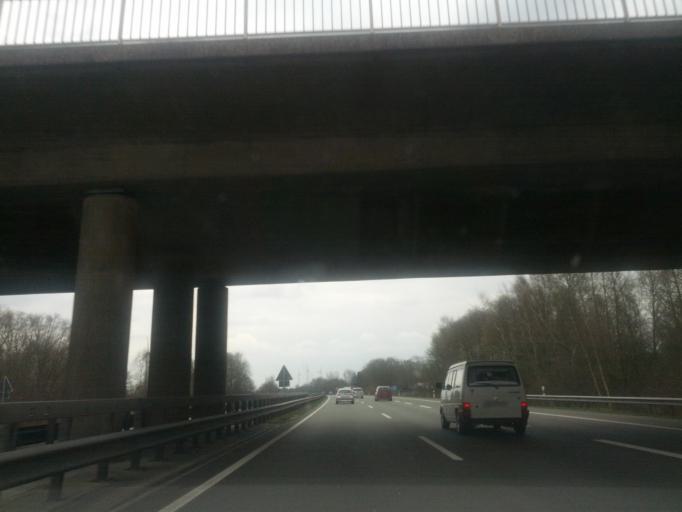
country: DE
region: Lower Saxony
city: Hatten
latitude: 53.0627
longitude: 8.3537
